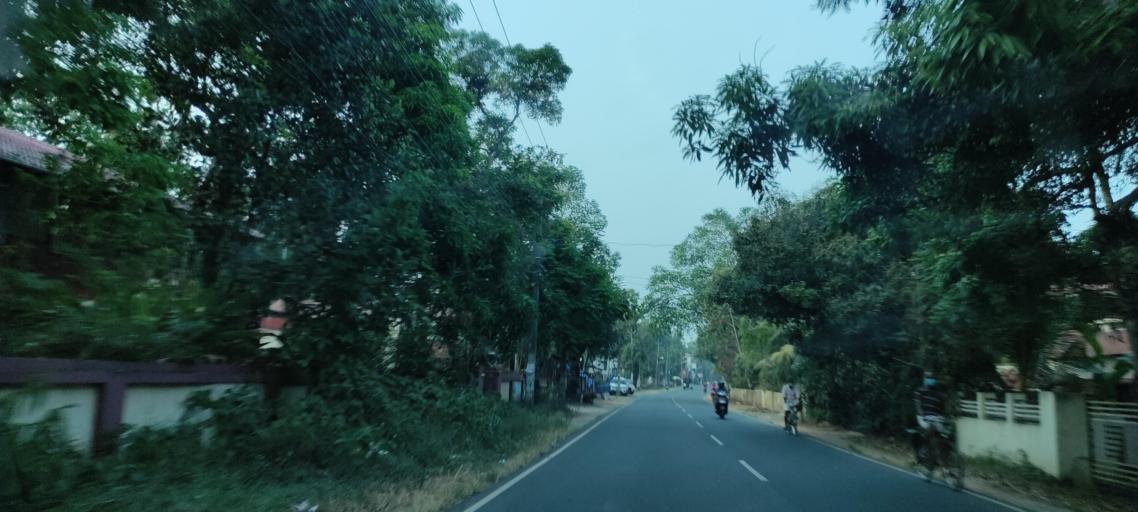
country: IN
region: Kerala
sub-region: Alappuzha
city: Mavelikara
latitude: 9.2961
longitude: 76.5331
